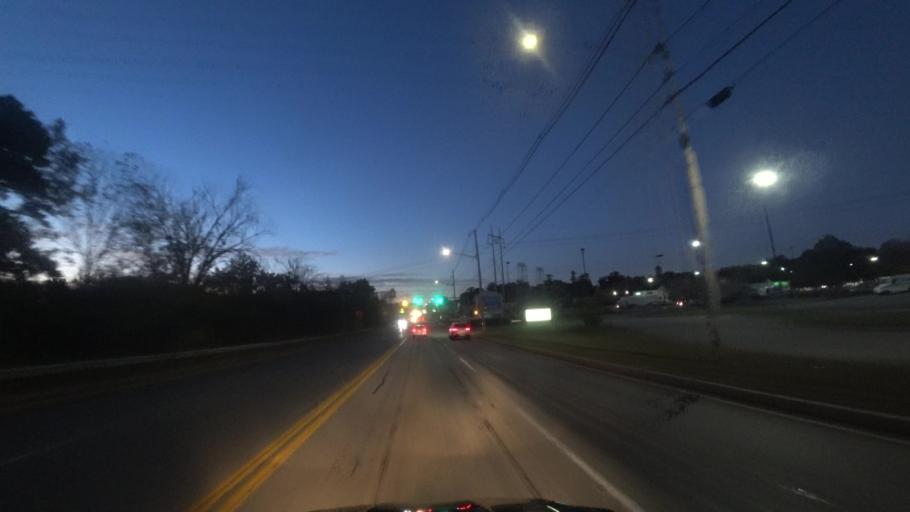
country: US
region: Massachusetts
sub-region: Middlesex County
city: North Reading
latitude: 42.5729
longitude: -71.1102
